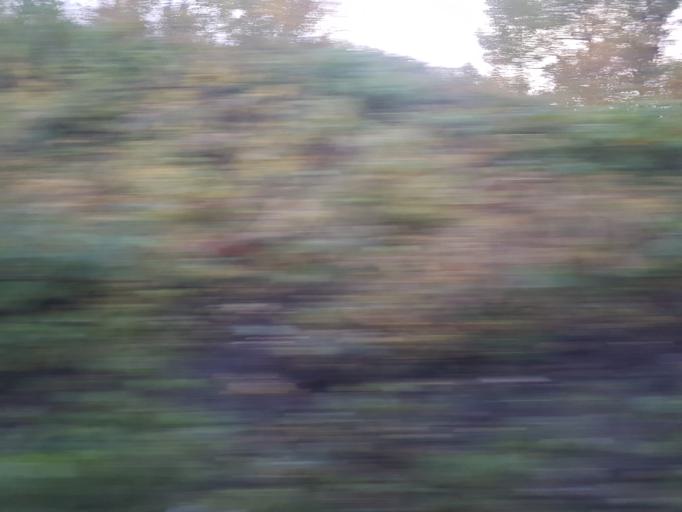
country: NO
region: Oppland
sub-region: Dovre
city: Dombas
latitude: 62.0507
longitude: 9.1380
